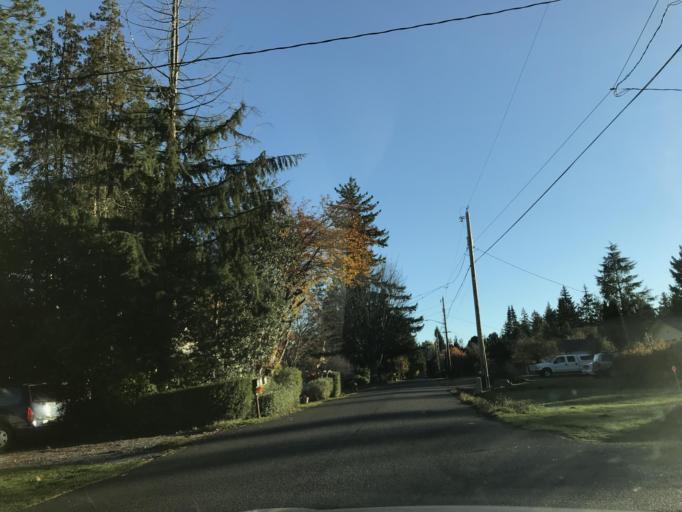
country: US
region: Washington
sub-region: Whatcom County
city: Geneva
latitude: 48.7461
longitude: -122.4306
